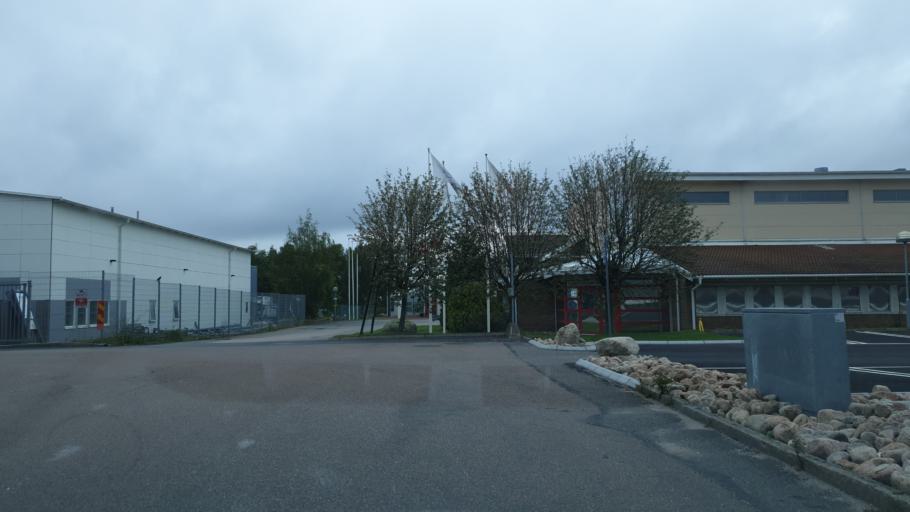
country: SE
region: Vaestra Goetaland
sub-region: Molndal
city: Moelndal
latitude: 57.6402
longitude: 11.9615
